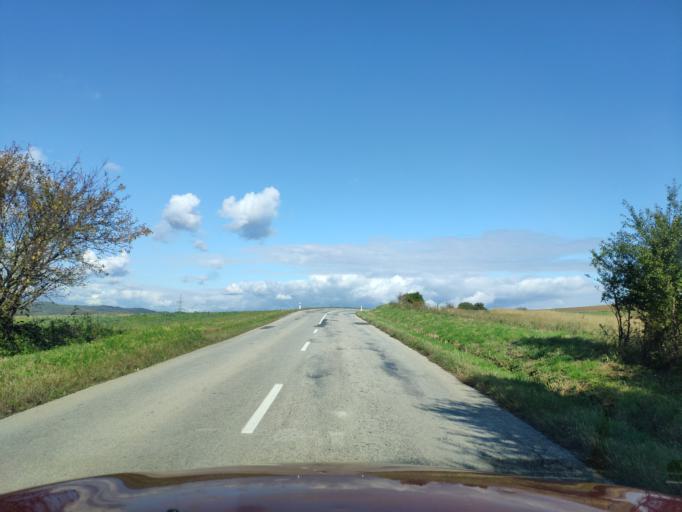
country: SK
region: Presovsky
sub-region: Okres Presov
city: Presov
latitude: 48.8945
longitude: 21.2592
